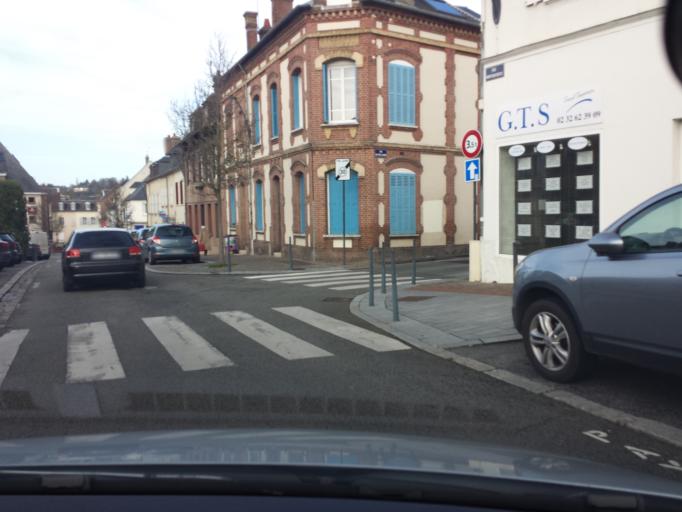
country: FR
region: Haute-Normandie
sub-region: Departement de l'Eure
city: Evreux
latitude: 49.0218
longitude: 1.1530
